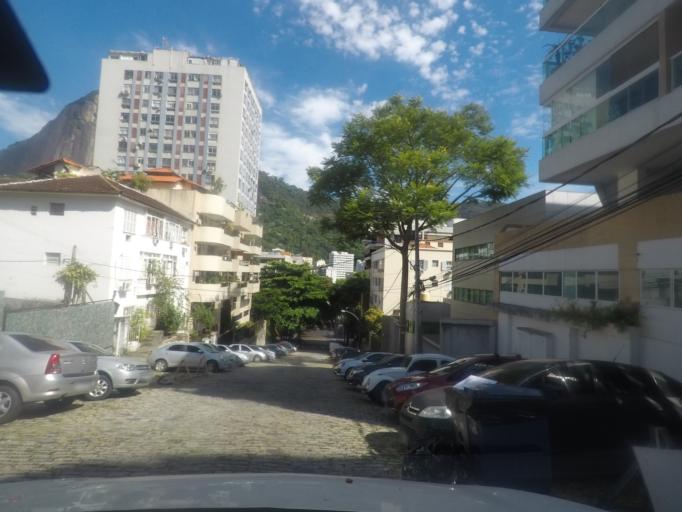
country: BR
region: Rio de Janeiro
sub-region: Rio De Janeiro
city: Rio de Janeiro
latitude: -22.9595
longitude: -43.1982
